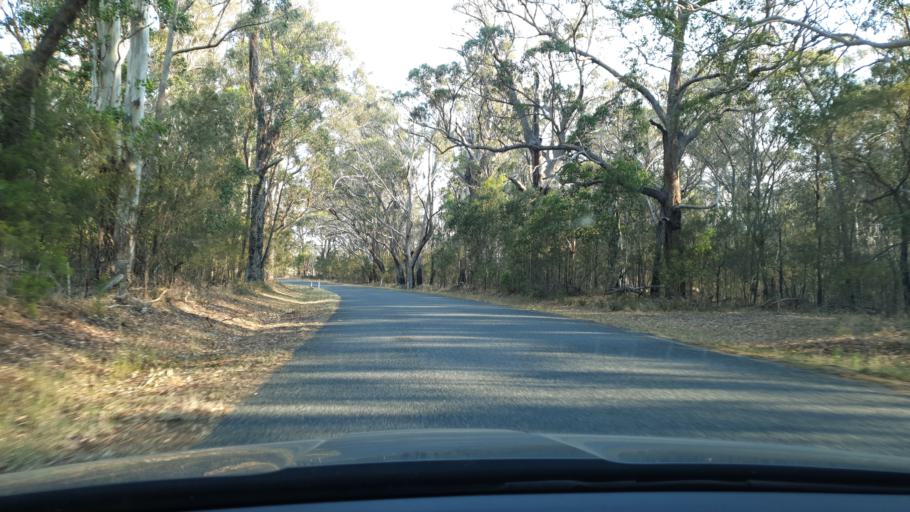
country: AU
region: New South Wales
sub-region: Tenterfield Municipality
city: Carrolls Creek
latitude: -28.6952
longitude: 152.0910
